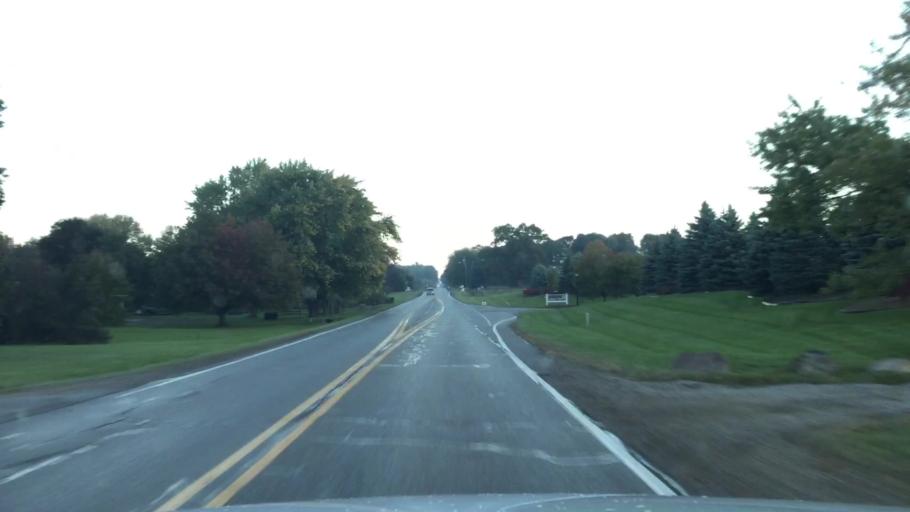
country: US
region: Michigan
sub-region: Livingston County
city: Howell
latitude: 42.6486
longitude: -83.9352
